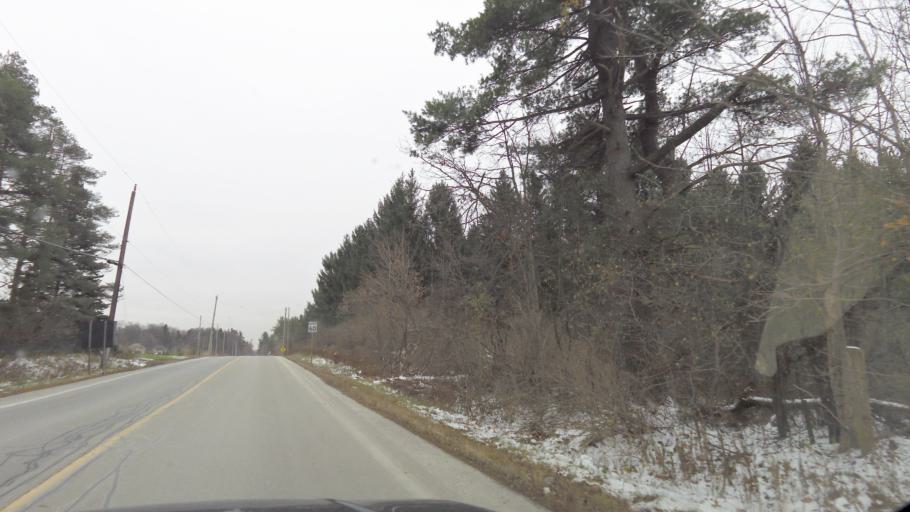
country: CA
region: Ontario
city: Vaughan
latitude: 43.8360
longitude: -79.5855
